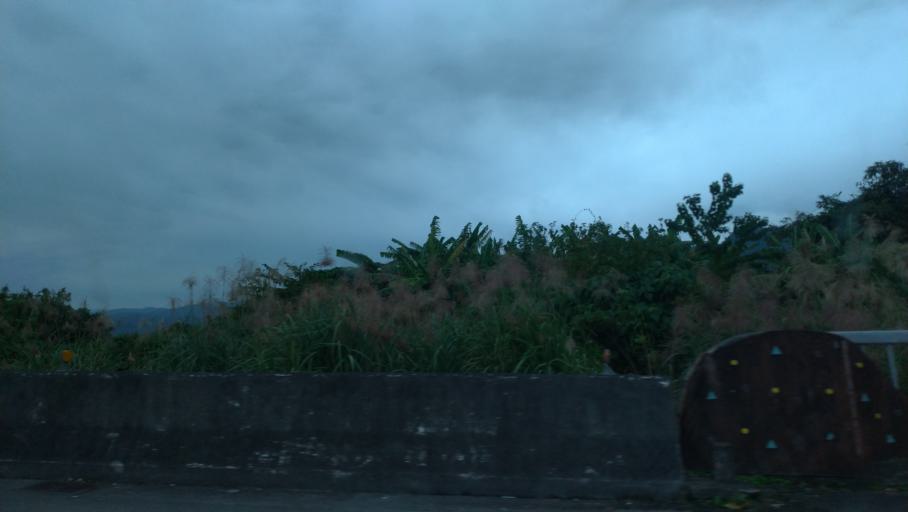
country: TW
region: Taiwan
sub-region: Yilan
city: Yilan
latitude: 24.8303
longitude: 121.8020
